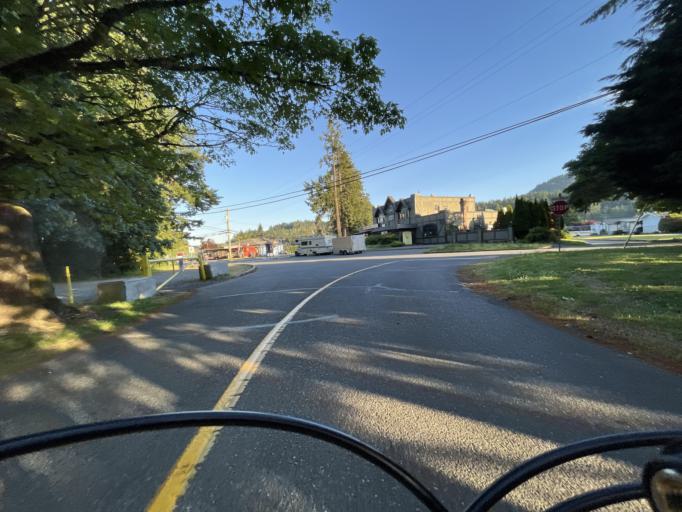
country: CA
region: British Columbia
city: Langford
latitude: 48.4596
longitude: -123.5536
